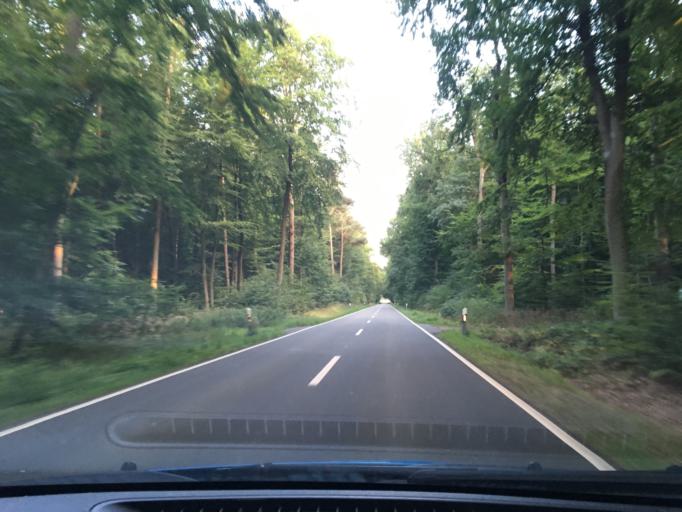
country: DE
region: Lower Saxony
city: Tosterglope
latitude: 53.2277
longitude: 10.8041
